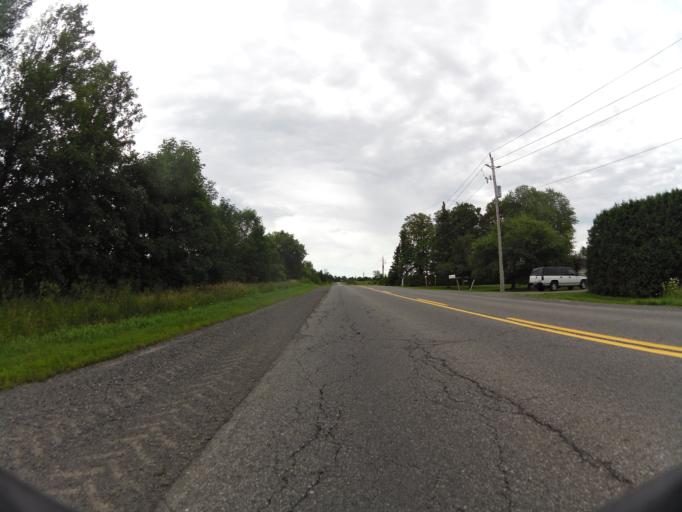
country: CA
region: Ontario
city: Ottawa
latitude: 45.2578
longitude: -75.6723
